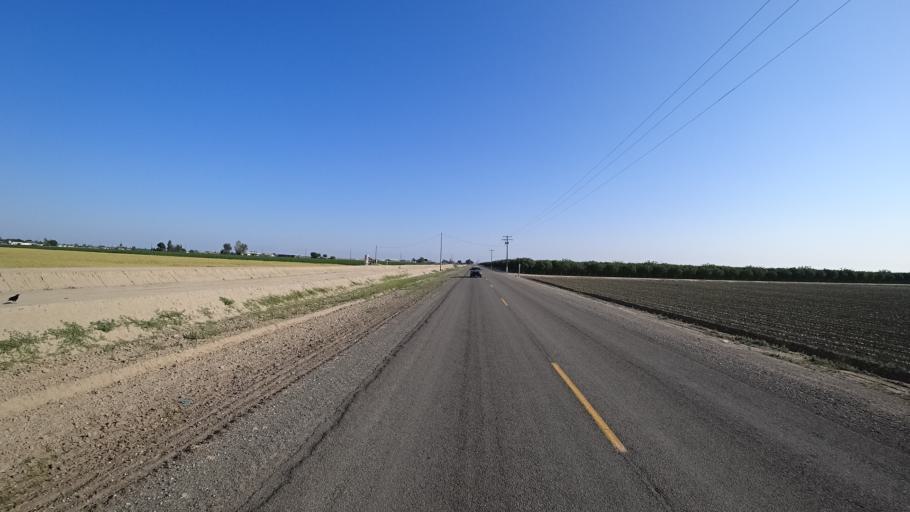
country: US
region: California
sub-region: Kings County
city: Home Garden
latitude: 36.3087
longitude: -119.5652
